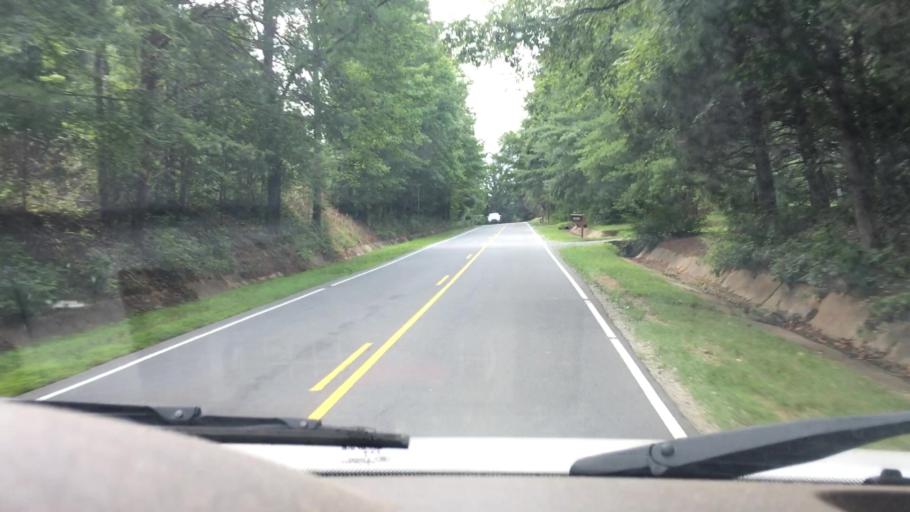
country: US
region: North Carolina
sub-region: Gaston County
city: Davidson
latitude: 35.4735
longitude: -80.7946
